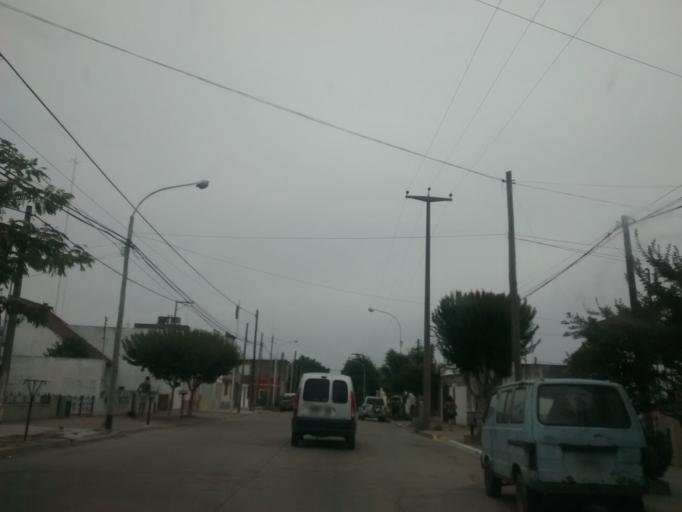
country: AR
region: Buenos Aires
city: Necochea
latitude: -38.5611
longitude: -58.7285
